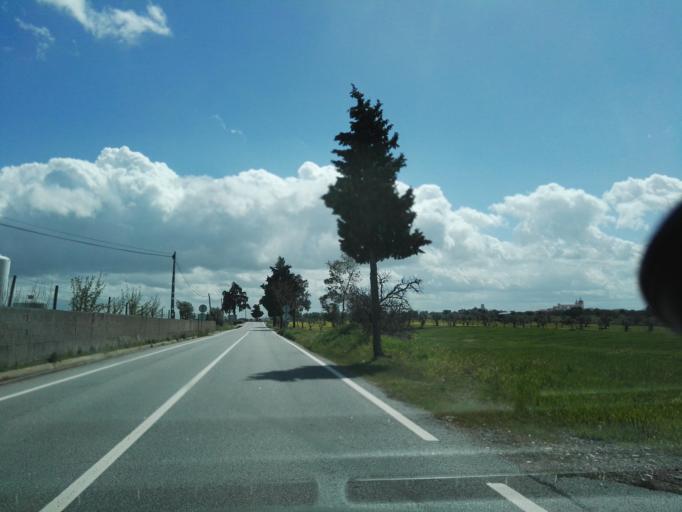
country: PT
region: Portalegre
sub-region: Arronches
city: Arronches
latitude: 39.1322
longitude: -7.2880
